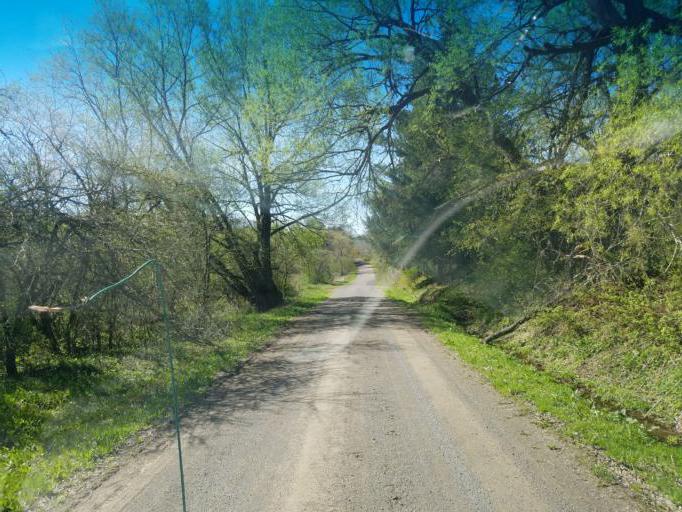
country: US
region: New York
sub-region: Allegany County
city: Andover
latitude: 41.9657
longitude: -77.7826
